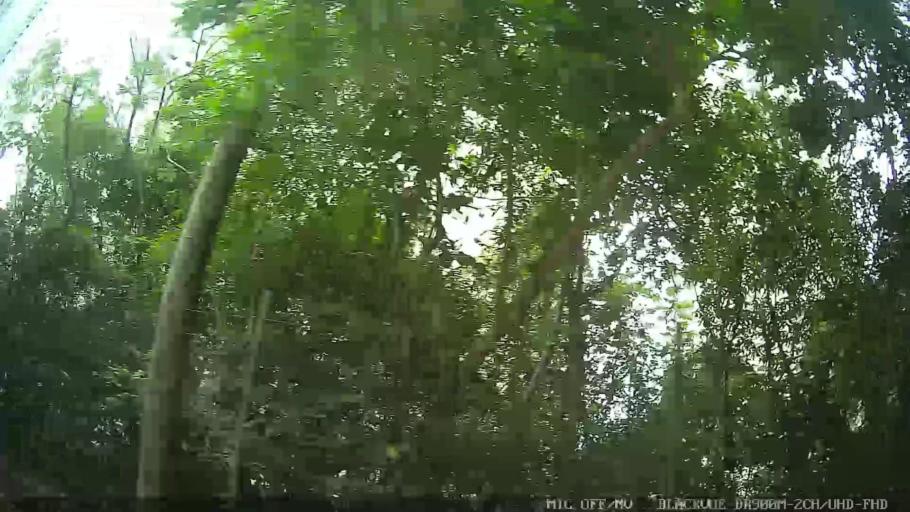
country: BR
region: Sao Paulo
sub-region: Guaruja
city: Guaruja
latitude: -23.9931
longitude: -46.1985
